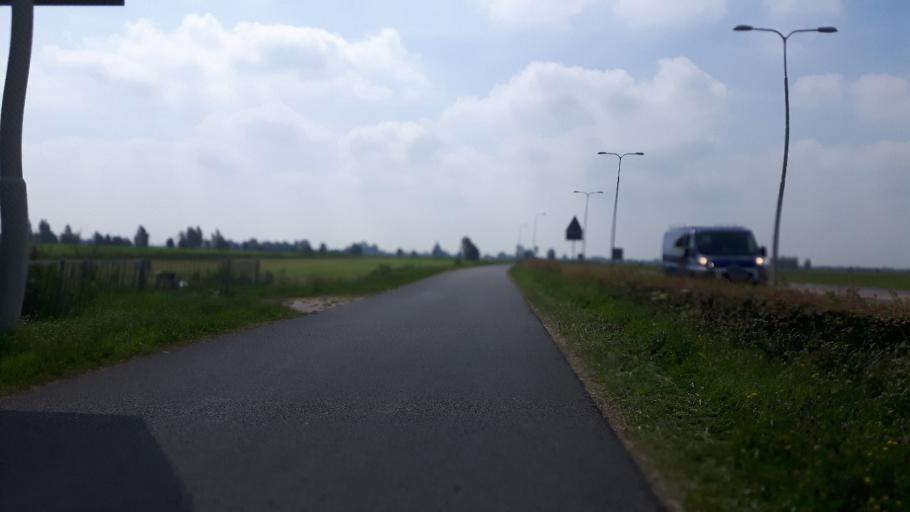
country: NL
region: Utrecht
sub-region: Gemeente Montfoort
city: Montfoort
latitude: 52.0355
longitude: 4.9378
